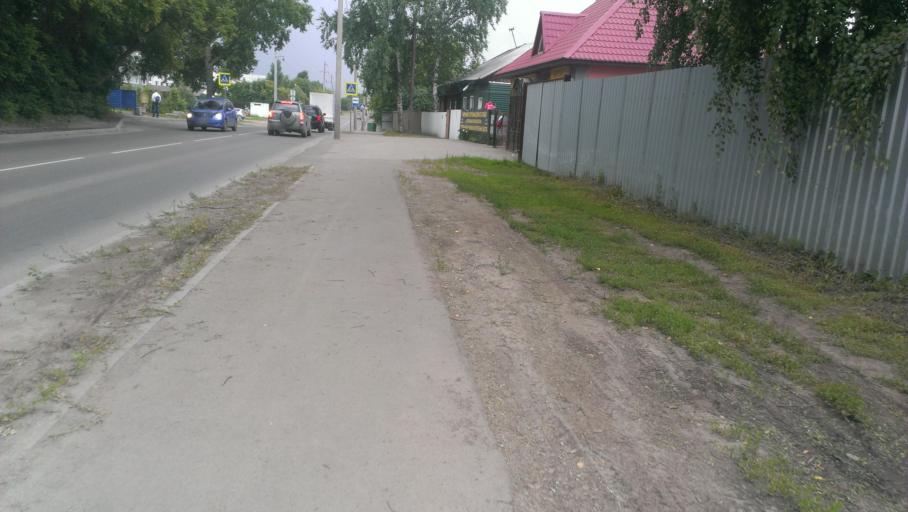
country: RU
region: Altai Krai
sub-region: Gorod Barnaulskiy
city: Barnaul
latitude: 53.3332
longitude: 83.7224
